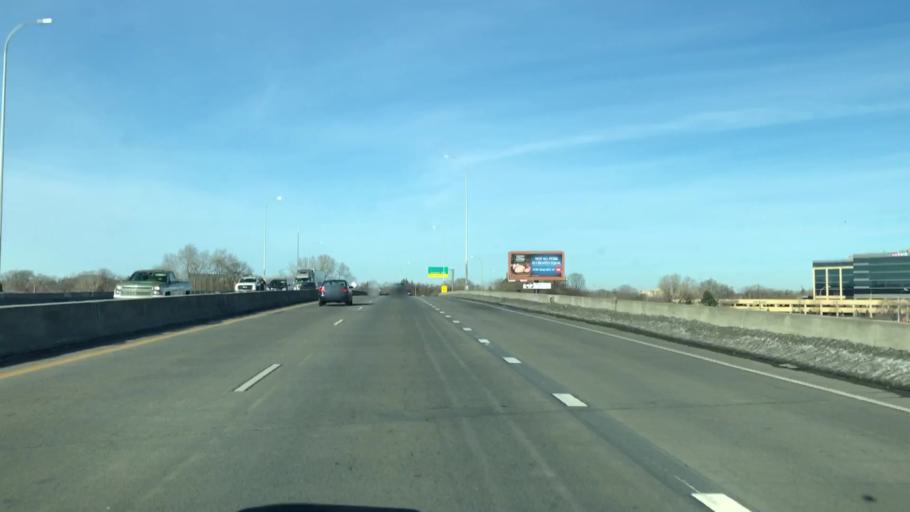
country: US
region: Minnesota
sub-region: Hennepin County
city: Minnetonka Mills
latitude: 44.9217
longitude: -93.4015
